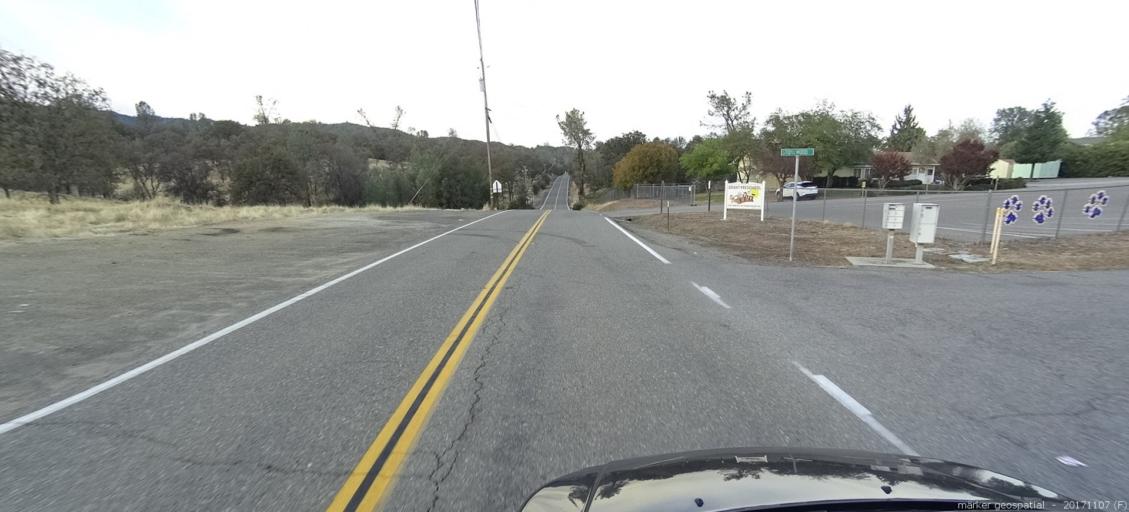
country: US
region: California
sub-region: Shasta County
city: Shasta
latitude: 40.5419
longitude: -122.4739
